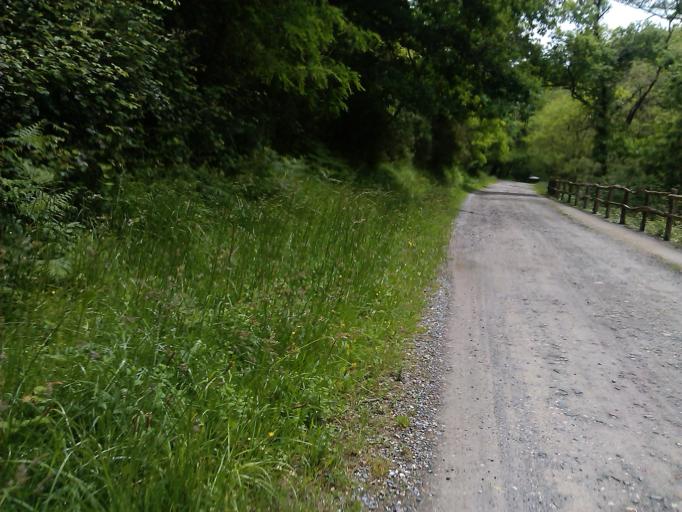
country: ES
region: Basque Country
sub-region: Provincia de Guipuzcoa
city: Andoain
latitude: 43.1874
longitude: -2.0034
